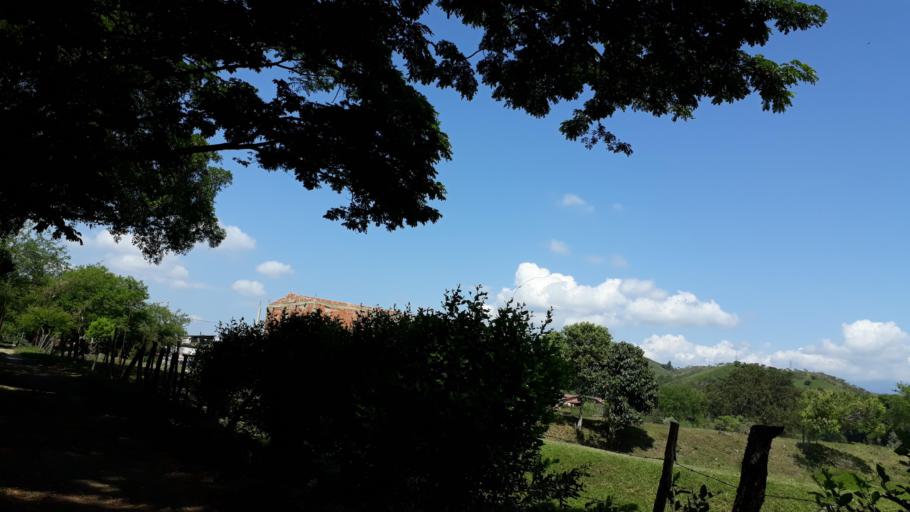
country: CO
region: Cauca
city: Buenos Aires
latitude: 3.1184
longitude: -76.6242
